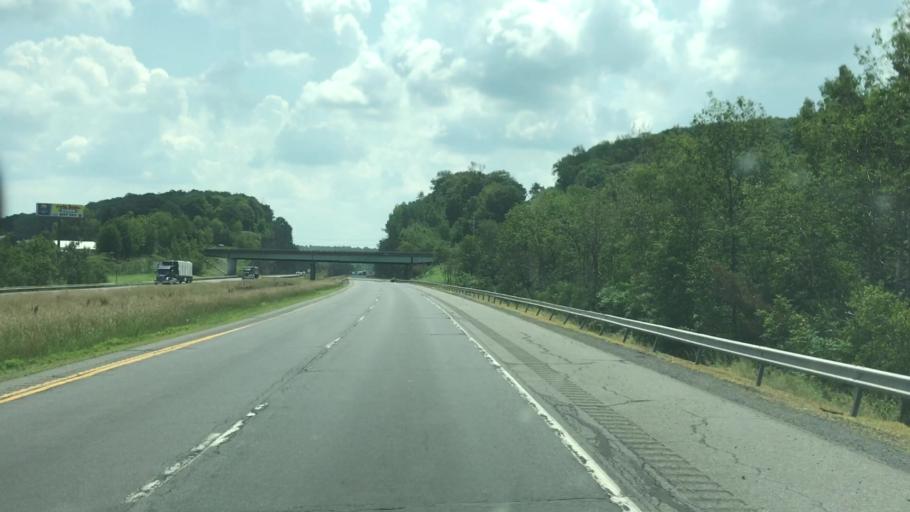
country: US
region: Pennsylvania
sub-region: Lackawanna County
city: Mount Cobb
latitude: 41.3978
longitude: -75.4838
